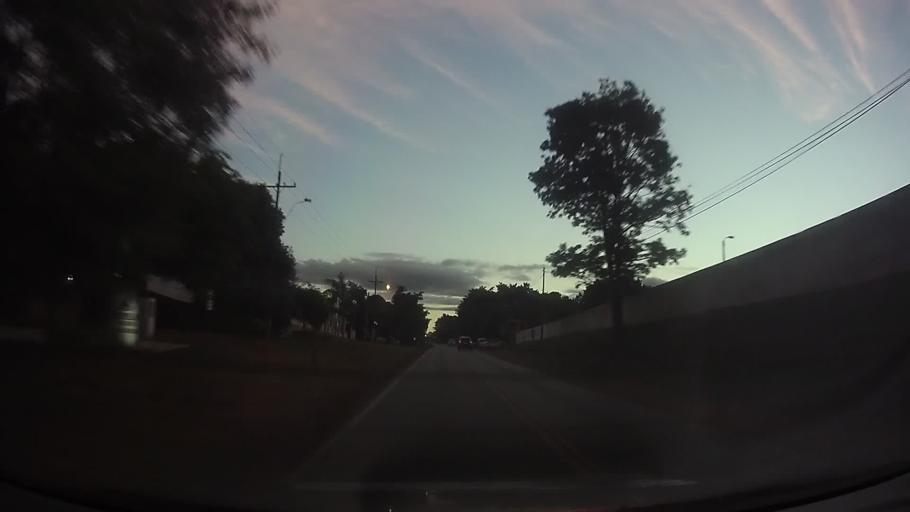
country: PY
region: Central
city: Ita
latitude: -25.4386
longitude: -57.3679
